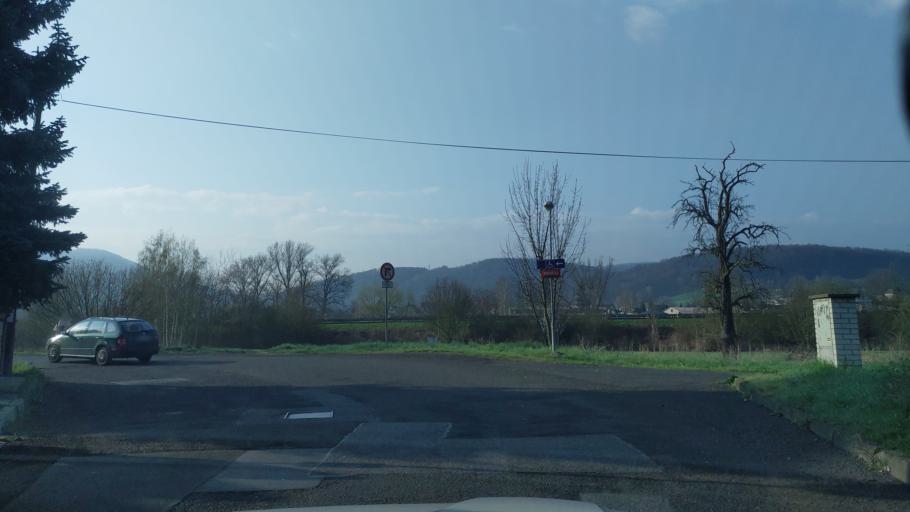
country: CZ
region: Ustecky
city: Velke Brezno
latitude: 50.6787
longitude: 14.1242
